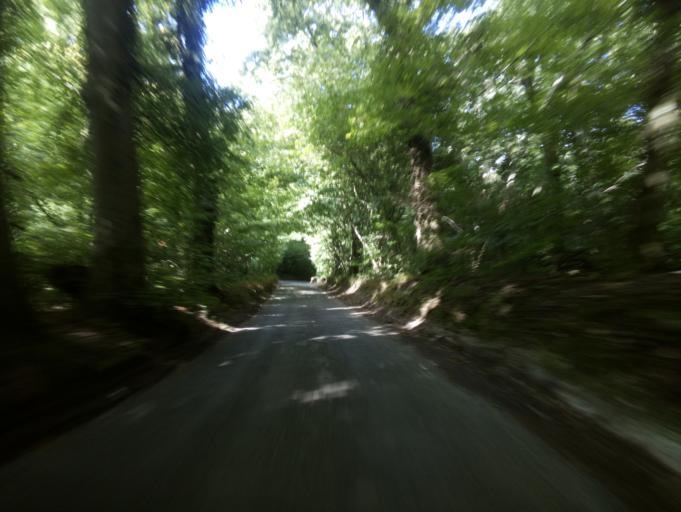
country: GB
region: England
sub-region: Hampshire
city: Chandlers Ford
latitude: 51.0635
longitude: -1.3804
